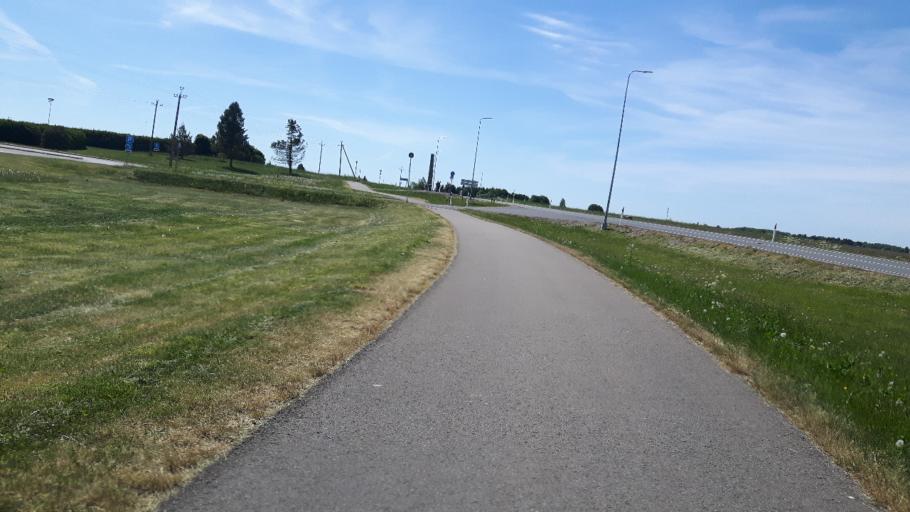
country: EE
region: Harju
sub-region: Kuusalu vald
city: Kuusalu
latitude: 59.4527
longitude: 25.4183
